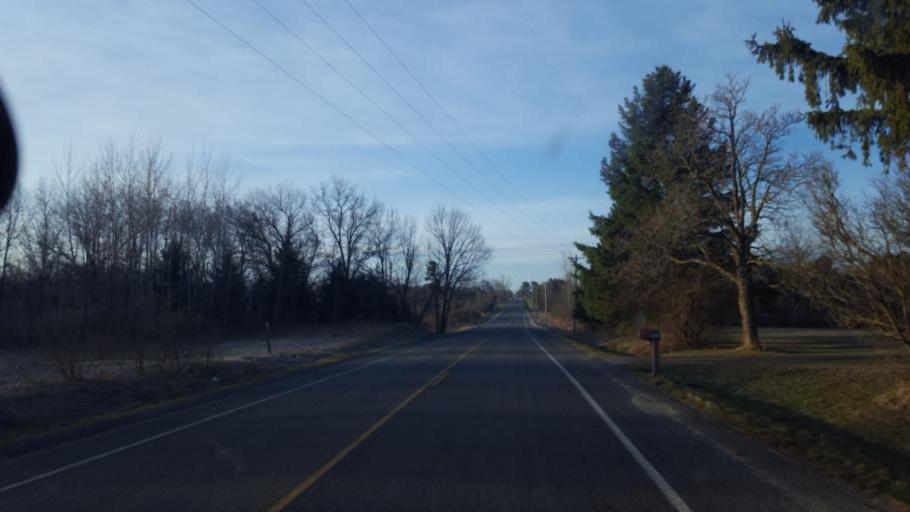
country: US
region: Michigan
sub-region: Montcalm County
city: Edmore
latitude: 43.4291
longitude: -85.0443
